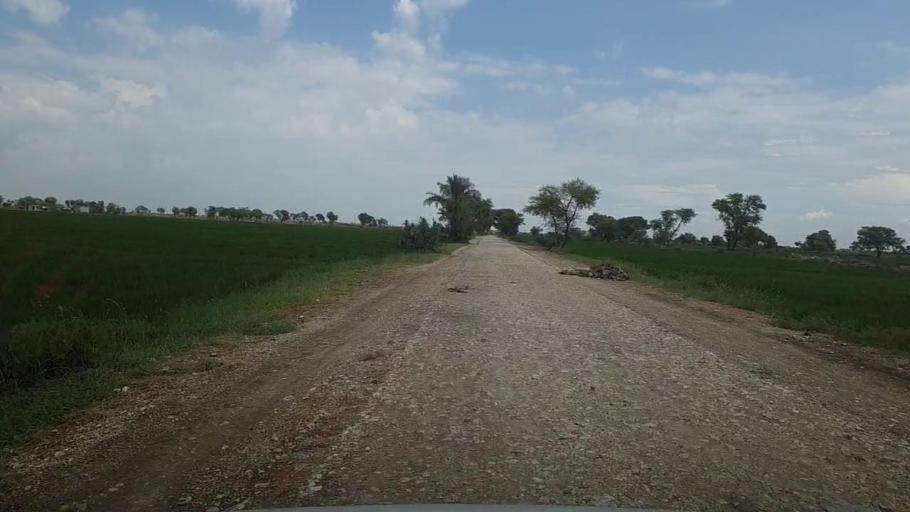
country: PK
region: Sindh
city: Kandhkot
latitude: 28.3421
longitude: 69.2175
